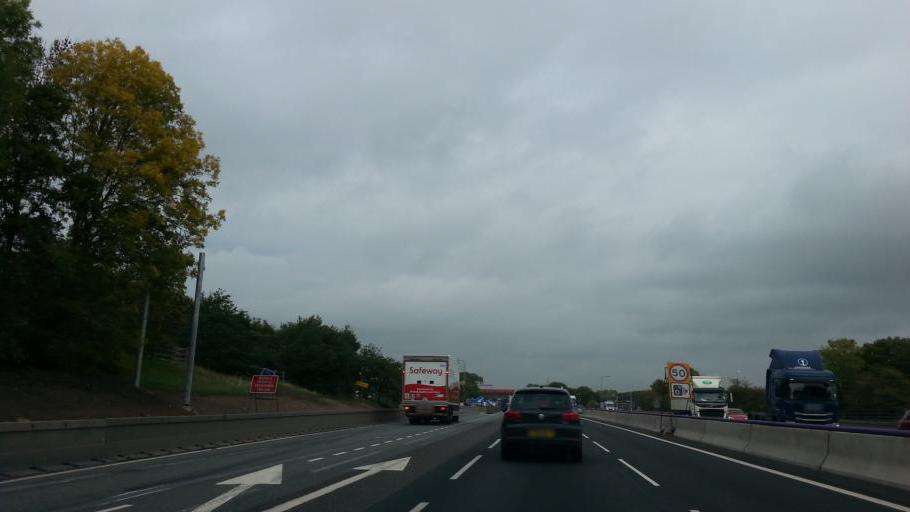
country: GB
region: England
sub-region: Cheshire East
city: Sandbach
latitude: 53.1360
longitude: -2.3362
